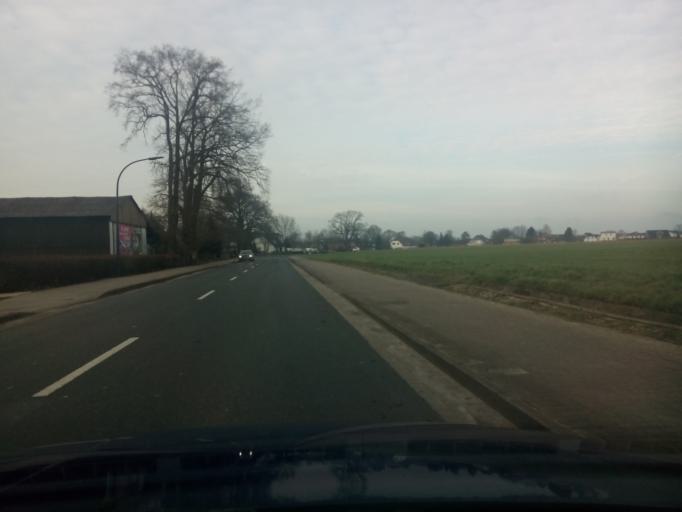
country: DE
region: Lower Saxony
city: Oyten
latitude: 53.0641
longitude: 9.0209
